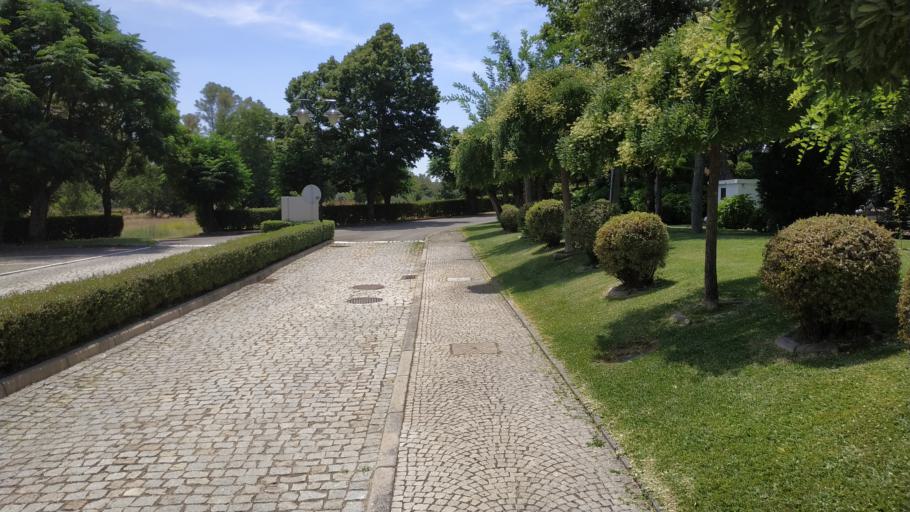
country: ES
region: Extremadura
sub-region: Provincia de Caceres
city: Zarza la Mayor
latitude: 40.0007
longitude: -6.8750
